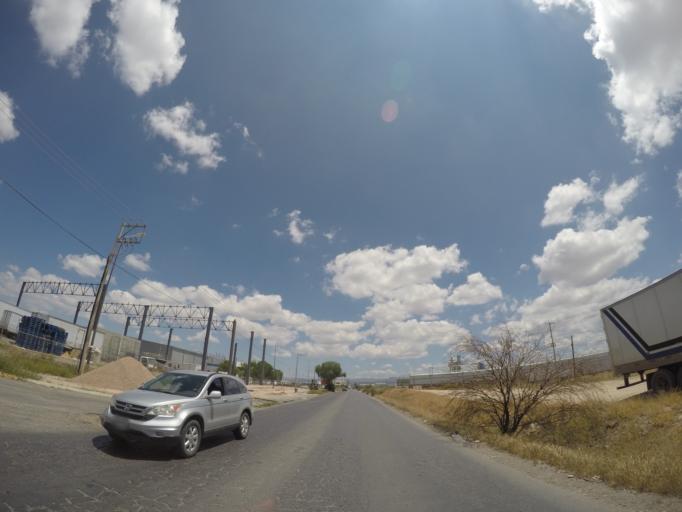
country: MX
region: San Luis Potosi
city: La Pila
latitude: 22.0433
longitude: -100.8823
